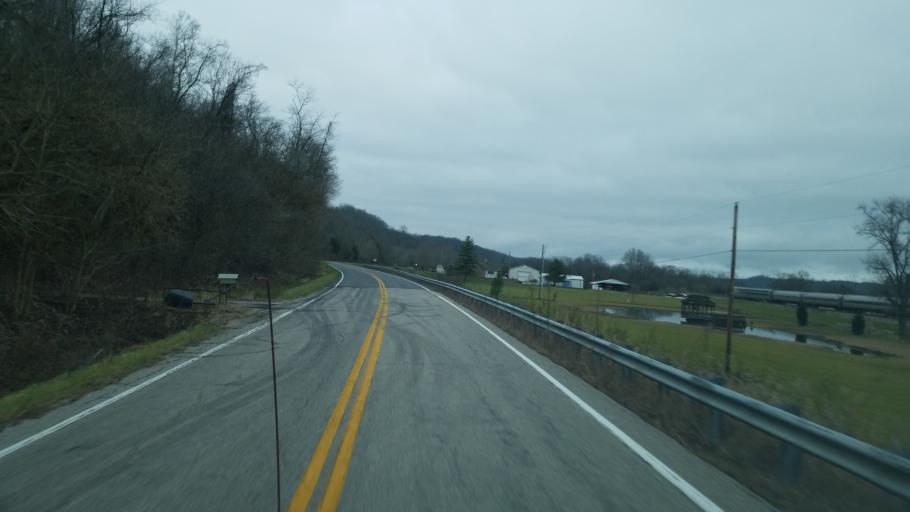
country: US
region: Kentucky
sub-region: Bracken County
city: Augusta
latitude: 38.7686
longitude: -84.0965
